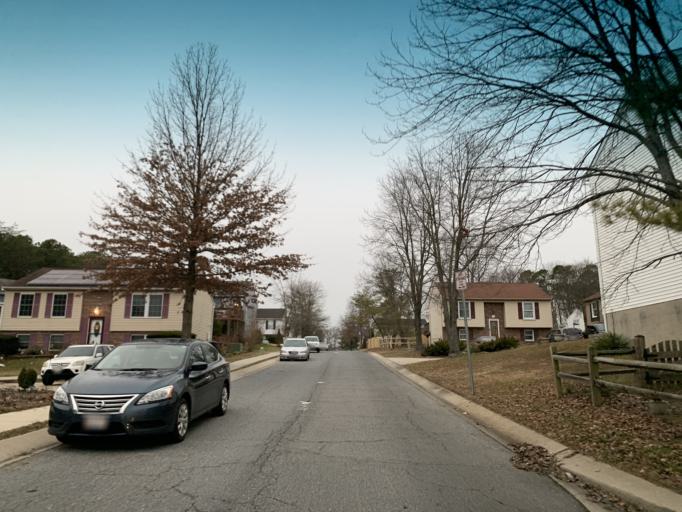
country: US
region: Maryland
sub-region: Baltimore County
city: White Marsh
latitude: 39.3818
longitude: -76.4504
